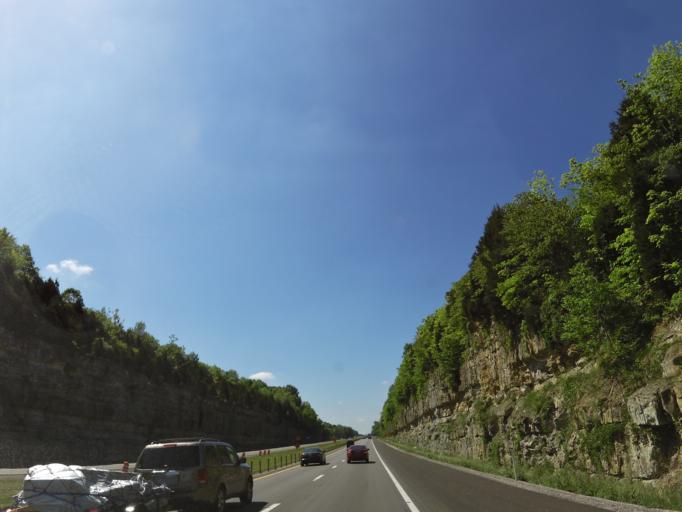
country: US
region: Kentucky
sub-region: Rockcastle County
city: Mount Vernon
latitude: 37.4192
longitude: -84.3421
